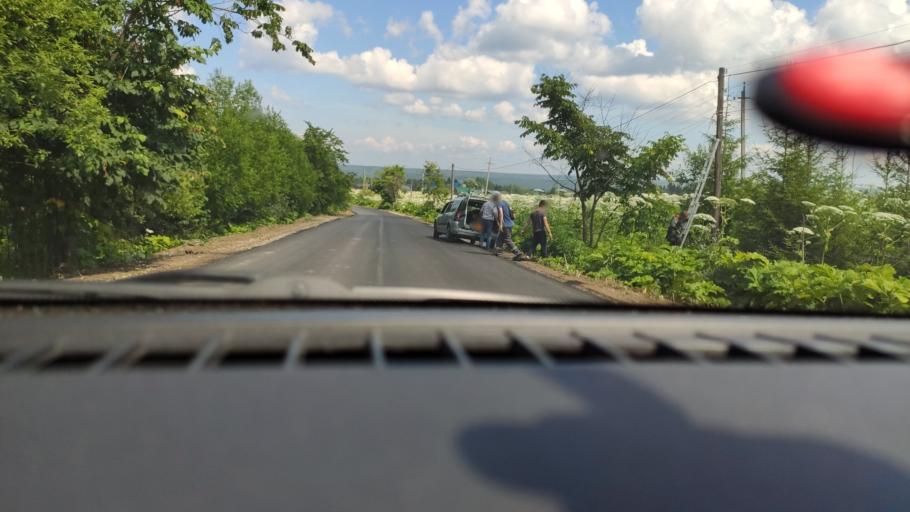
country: RU
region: Perm
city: Sylva
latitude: 58.0355
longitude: 56.7238
